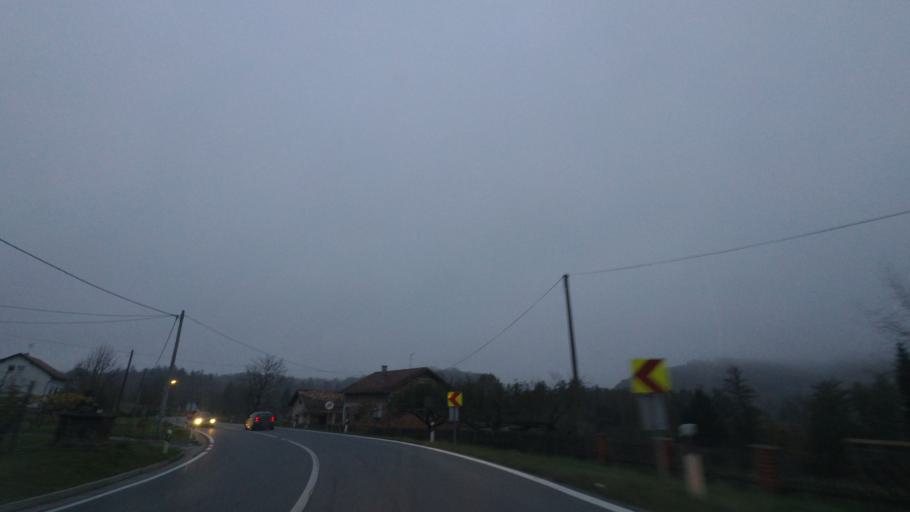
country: HR
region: Sisacko-Moslavacka
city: Petrinja
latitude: 45.4330
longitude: 16.2311
